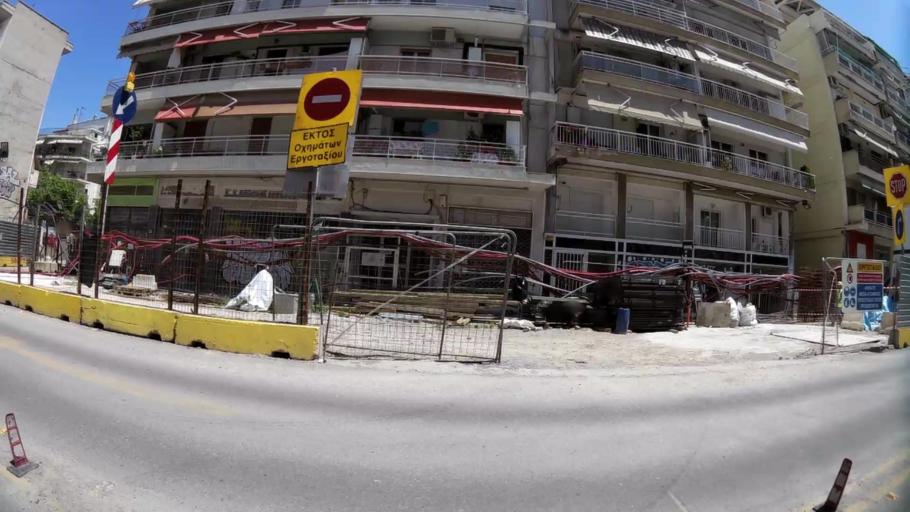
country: GR
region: Central Macedonia
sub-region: Nomos Thessalonikis
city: Triandria
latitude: 40.6054
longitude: 22.9582
